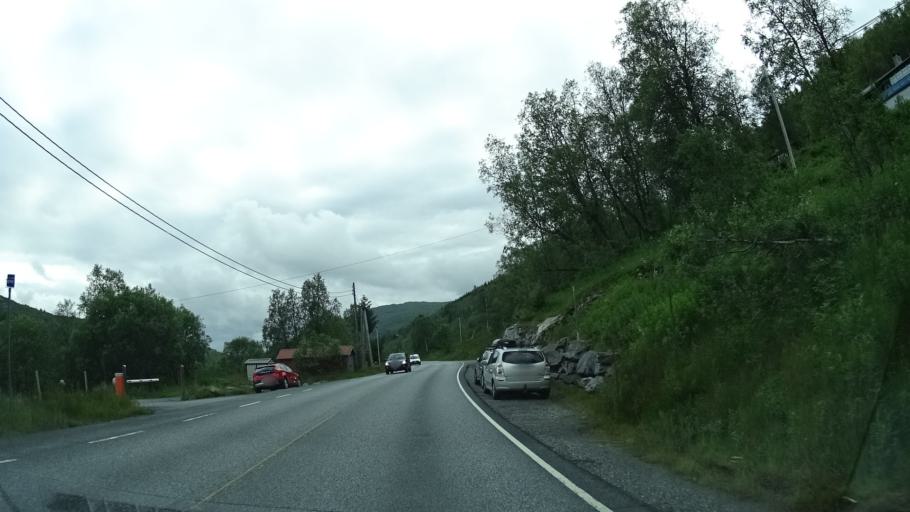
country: NO
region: Hordaland
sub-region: Samnanger
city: Tysse
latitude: 60.3939
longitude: 5.9472
